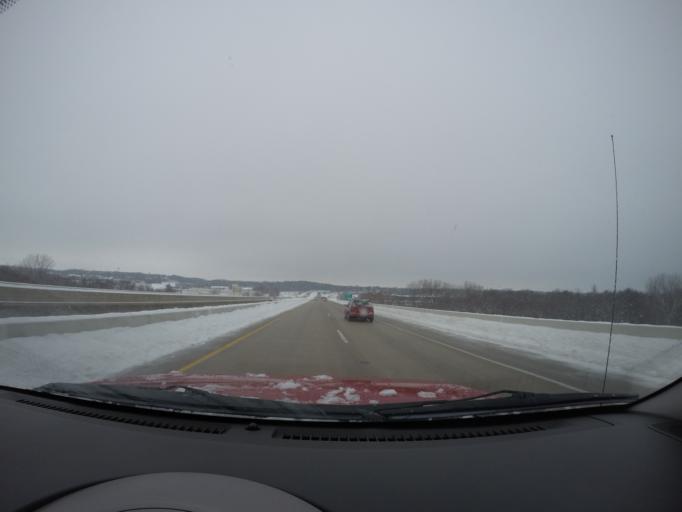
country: US
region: Minnesota
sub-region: Olmsted County
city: Rochester
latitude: 43.9743
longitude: -92.4518
